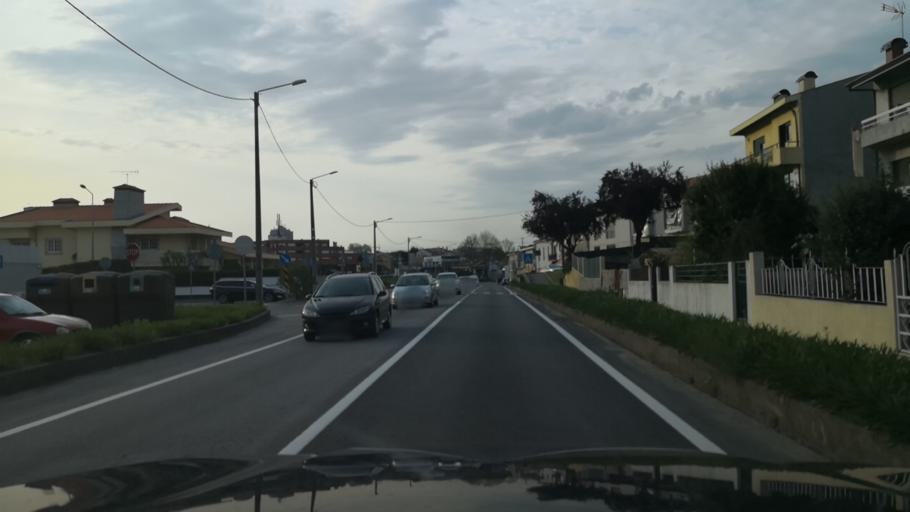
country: PT
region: Porto
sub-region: Valongo
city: Campo
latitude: 41.1864
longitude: -8.4877
